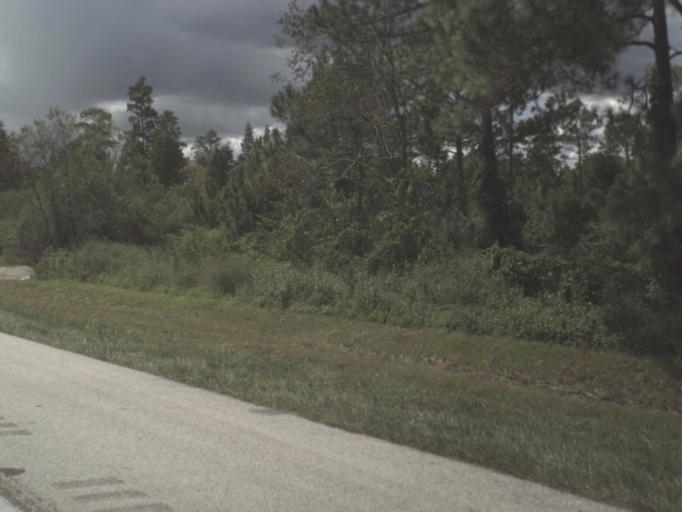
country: US
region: Florida
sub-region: Polk County
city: Polk City
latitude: 28.1859
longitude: -81.7347
